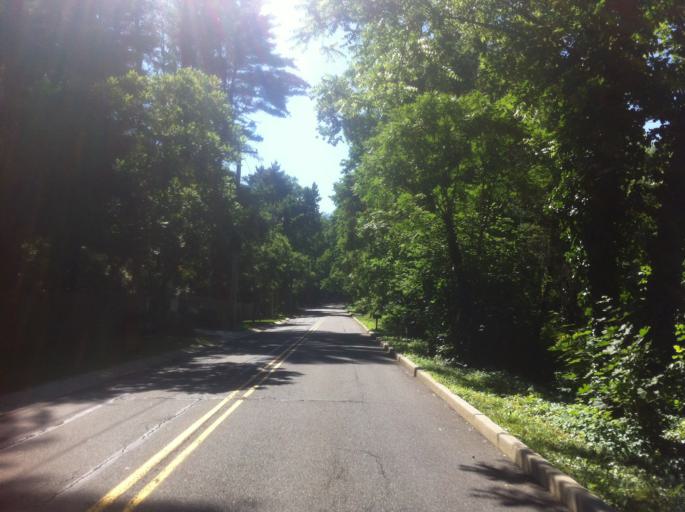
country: US
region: New York
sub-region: Nassau County
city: Upper Brookville
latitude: 40.8277
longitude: -73.5681
